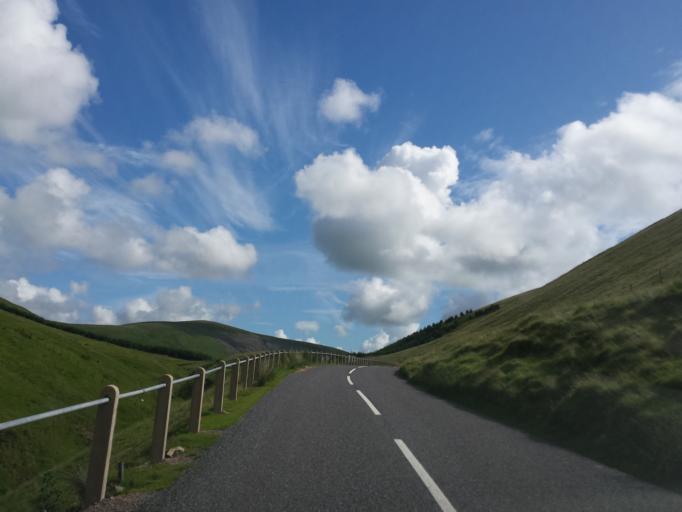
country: GB
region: Scotland
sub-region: Dumfries and Galloway
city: Moffat
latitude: 55.4275
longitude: -3.2684
